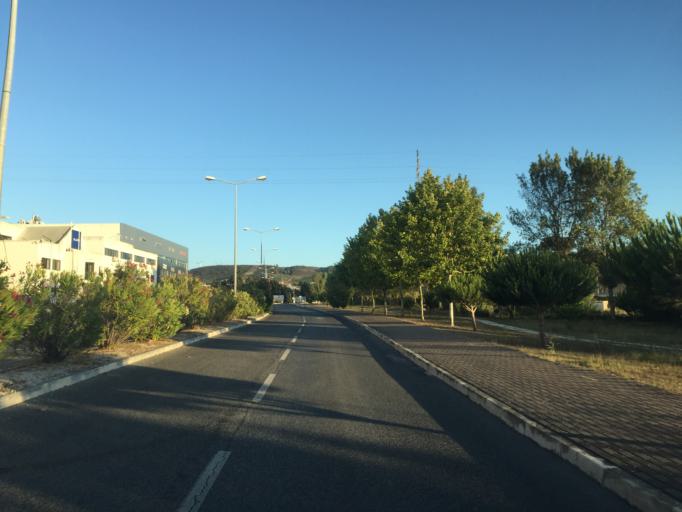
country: PT
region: Lisbon
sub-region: Torres Vedras
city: Torres Vedras
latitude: 39.0775
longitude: -9.2574
